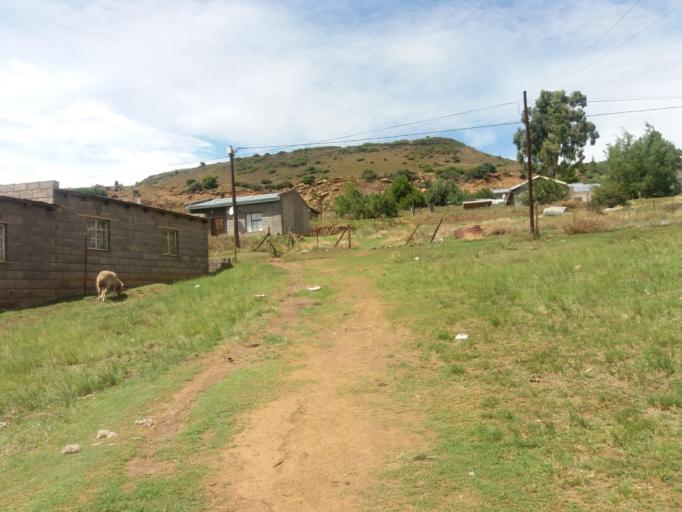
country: LS
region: Quthing
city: Quthing
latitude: -30.4111
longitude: 27.6950
